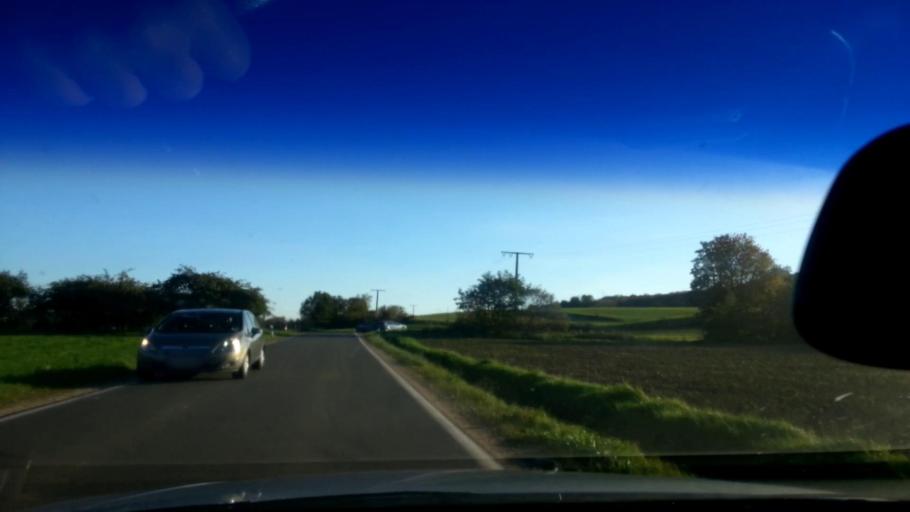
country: DE
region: Bavaria
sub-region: Upper Franconia
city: Rattelsdorf
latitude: 50.0130
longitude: 10.8726
